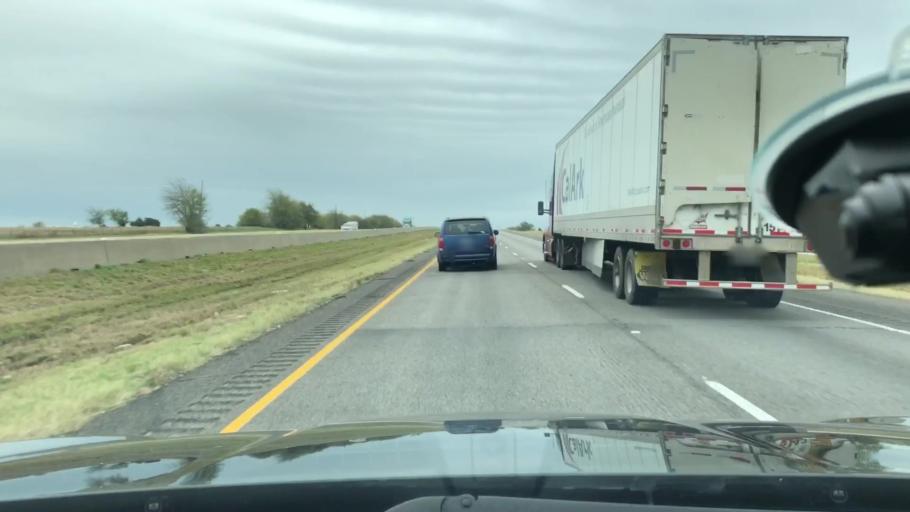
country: US
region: Texas
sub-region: Hunt County
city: Commerce
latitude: 33.1294
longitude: -95.8591
